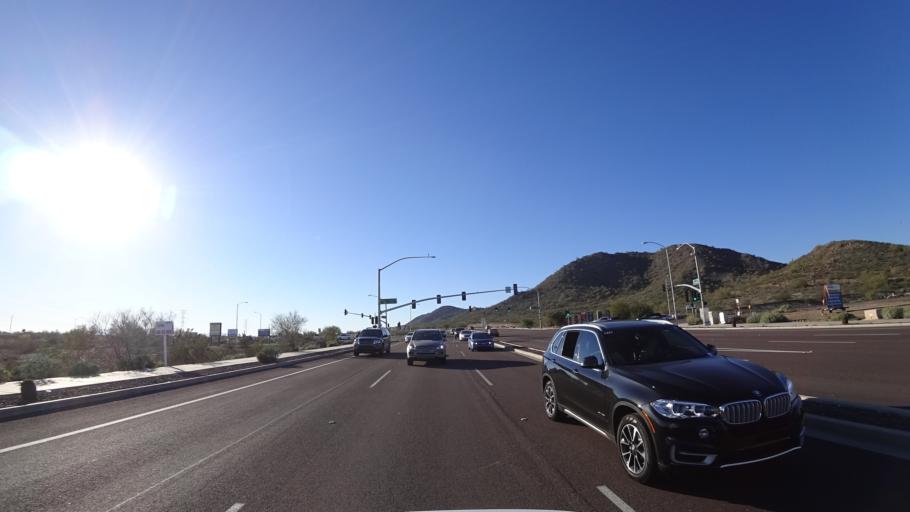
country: US
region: Arizona
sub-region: Maricopa County
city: Sun City West
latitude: 33.7091
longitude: -112.2352
